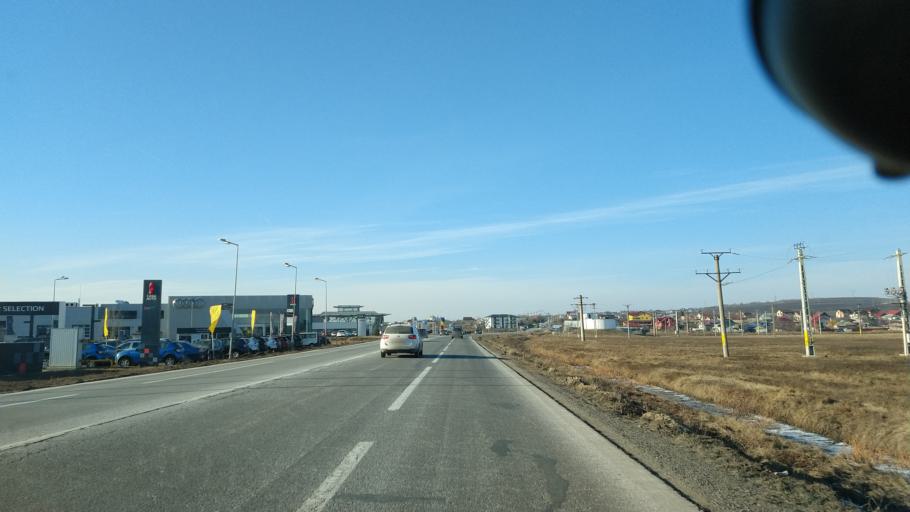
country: RO
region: Iasi
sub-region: Comuna Letcani
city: Letcani
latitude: 47.1894
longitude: 27.4333
